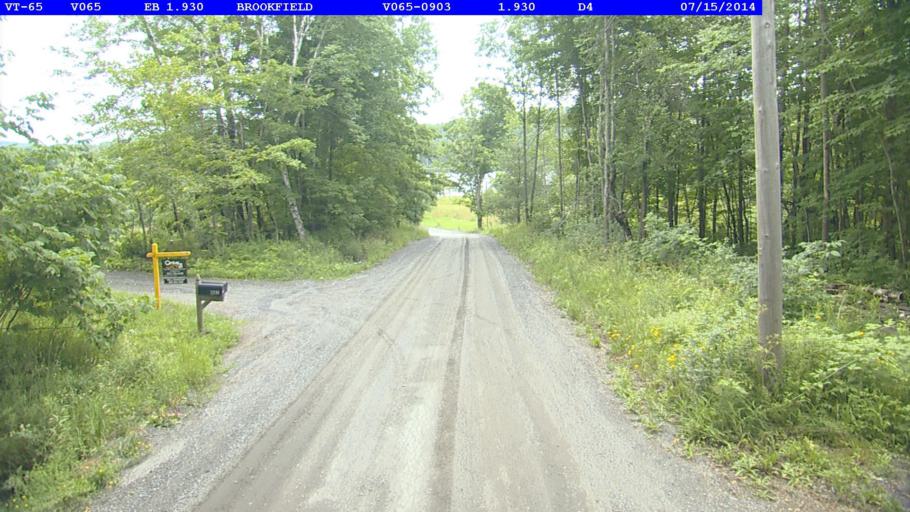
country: US
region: Vermont
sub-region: Washington County
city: Northfield
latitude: 44.0436
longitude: -72.6241
